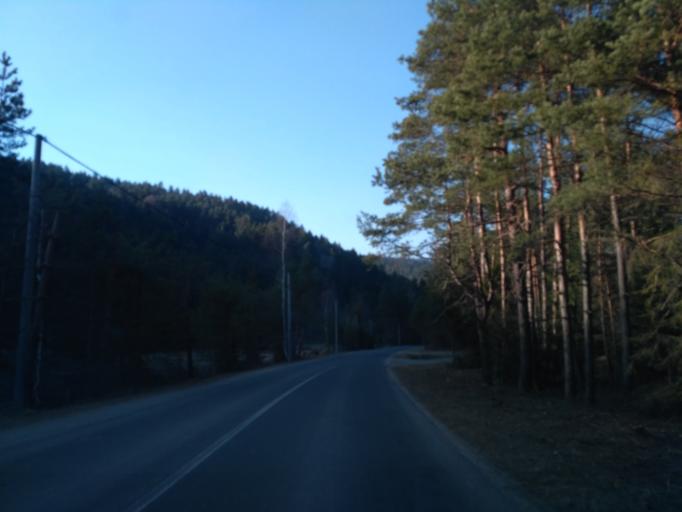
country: SK
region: Kosicky
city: Medzev
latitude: 48.7547
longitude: 20.7770
